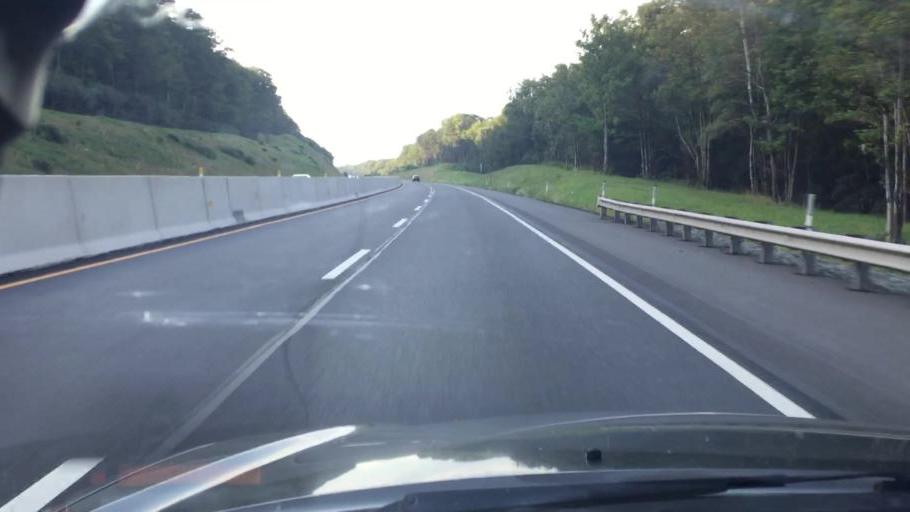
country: US
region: Pennsylvania
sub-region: Carbon County
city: Towamensing Trails
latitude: 41.0110
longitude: -75.6373
